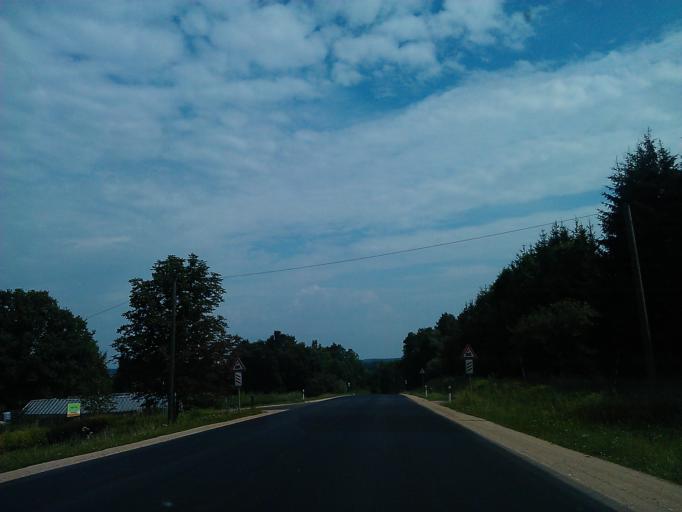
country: LV
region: Priekuli
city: Priekuli
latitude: 57.3317
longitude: 25.3182
